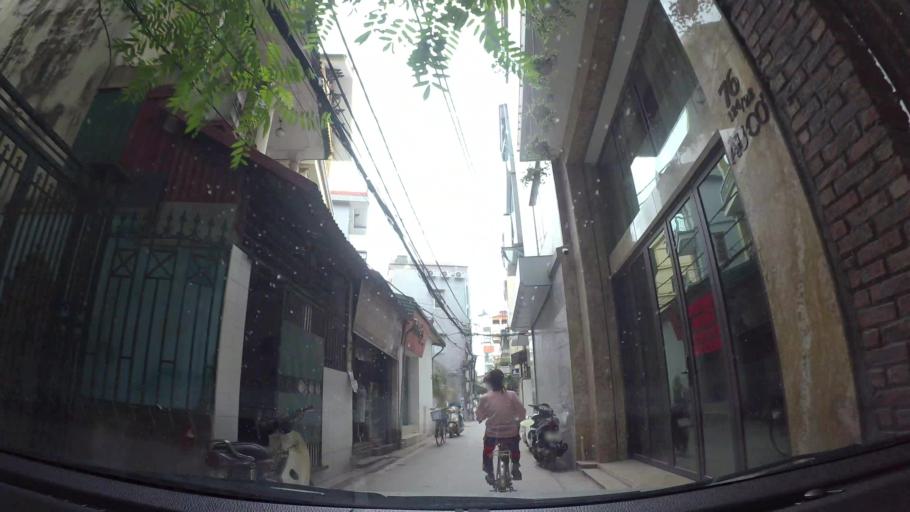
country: VN
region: Ha Noi
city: Tay Ho
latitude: 21.0616
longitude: 105.8363
